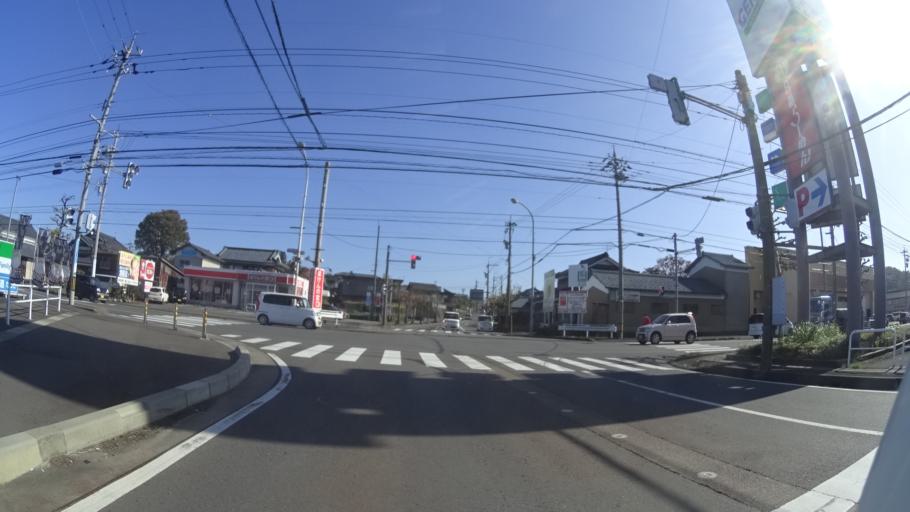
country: JP
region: Fukui
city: Sabae
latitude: 35.9639
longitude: 136.1755
